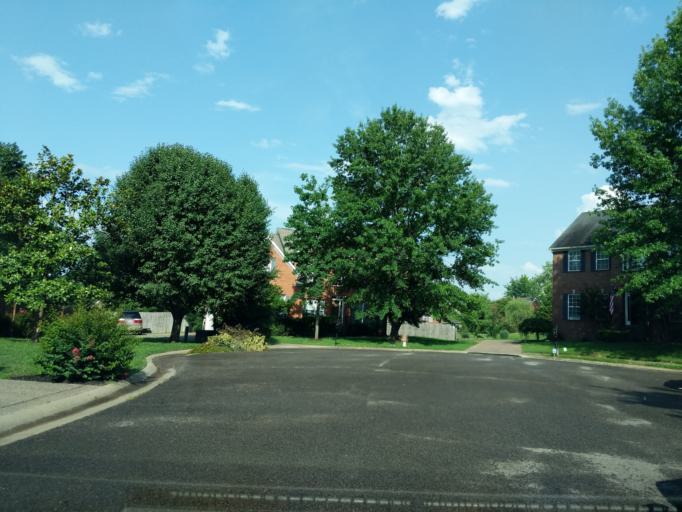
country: US
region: Tennessee
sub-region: Cheatham County
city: Pegram
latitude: 36.0367
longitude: -86.9593
